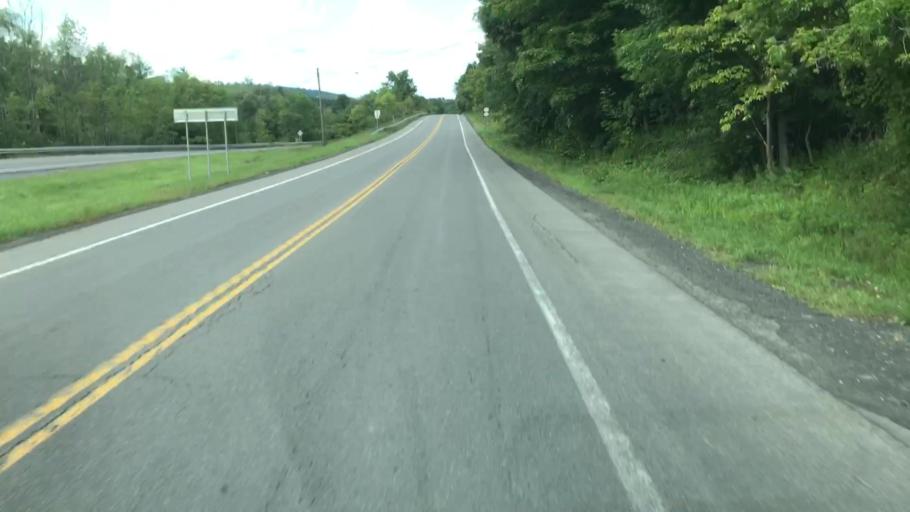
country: US
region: New York
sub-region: Onondaga County
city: Marcellus
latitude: 42.9634
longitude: -76.3357
